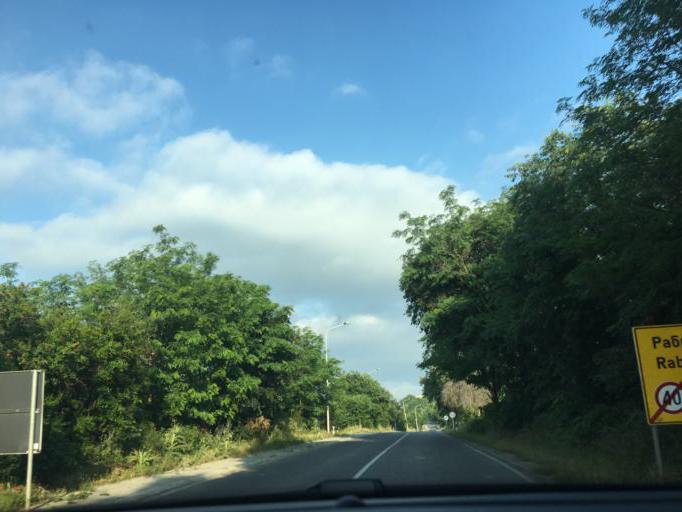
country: MK
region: Valandovo
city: Valandovo
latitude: 41.3189
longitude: 22.5775
